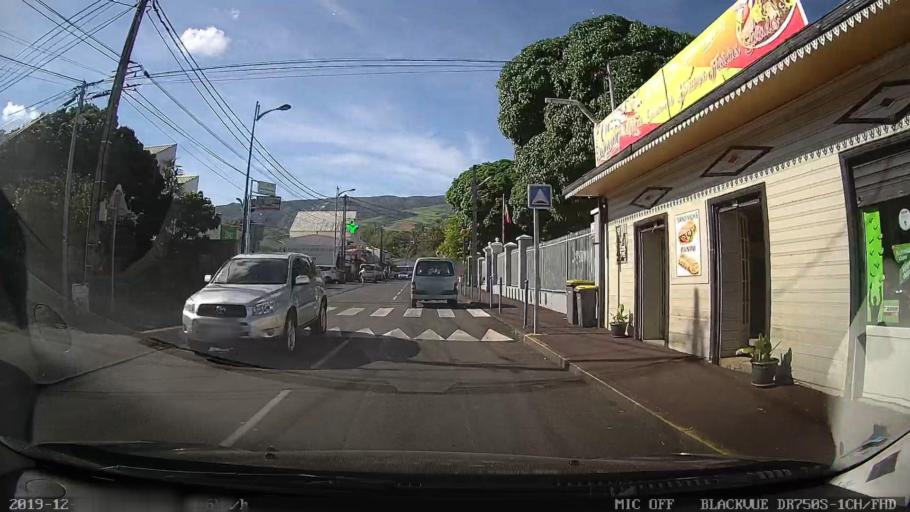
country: RE
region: Reunion
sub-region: Reunion
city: Sainte-Marie
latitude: -20.9151
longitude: 55.5100
